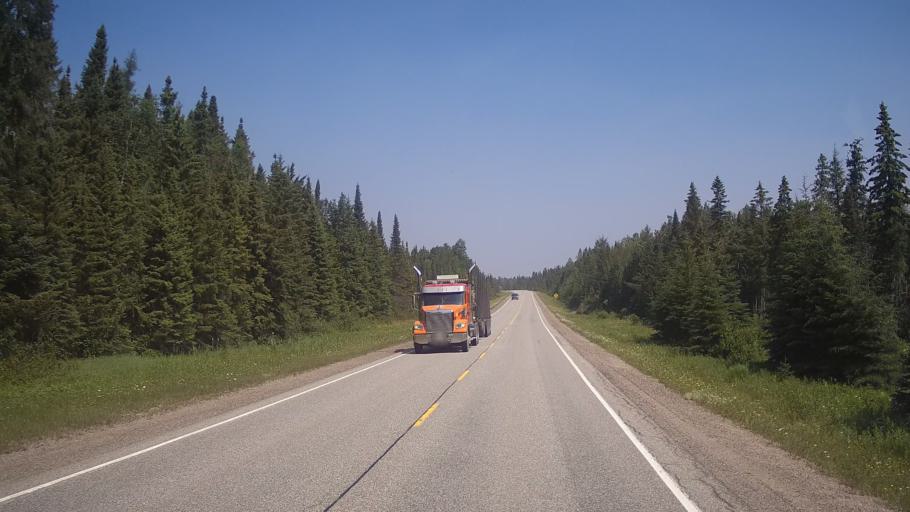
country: CA
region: Ontario
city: Timmins
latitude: 48.0952
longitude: -81.5927
